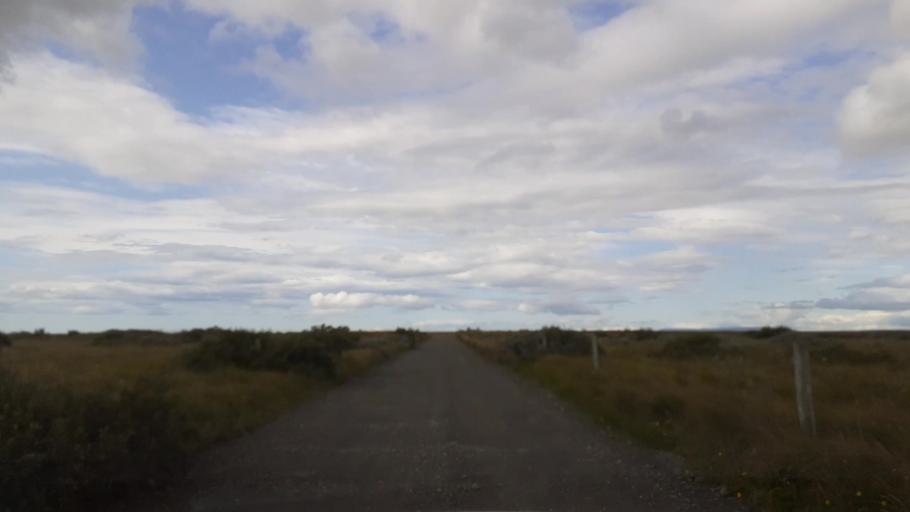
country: IS
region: South
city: Vestmannaeyjar
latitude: 63.8192
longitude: -20.4249
